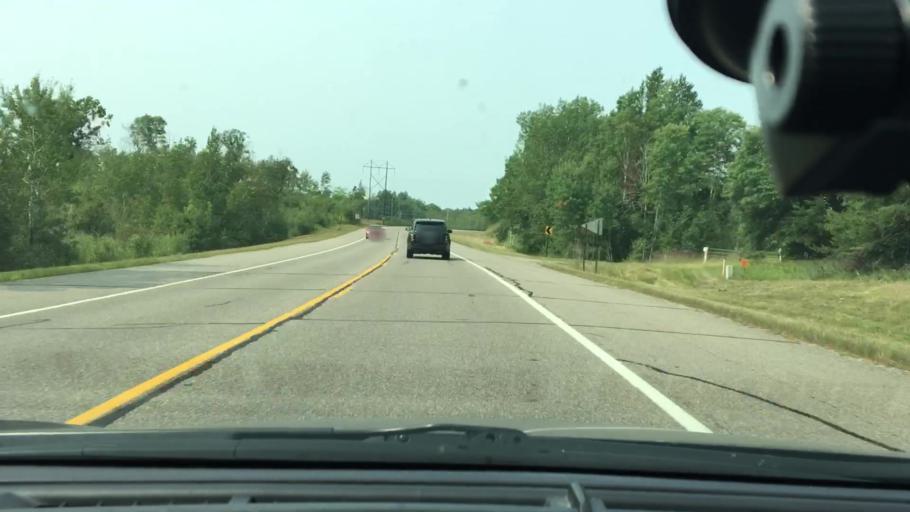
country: US
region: Minnesota
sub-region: Cass County
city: East Gull Lake
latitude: 46.3836
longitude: -94.3214
